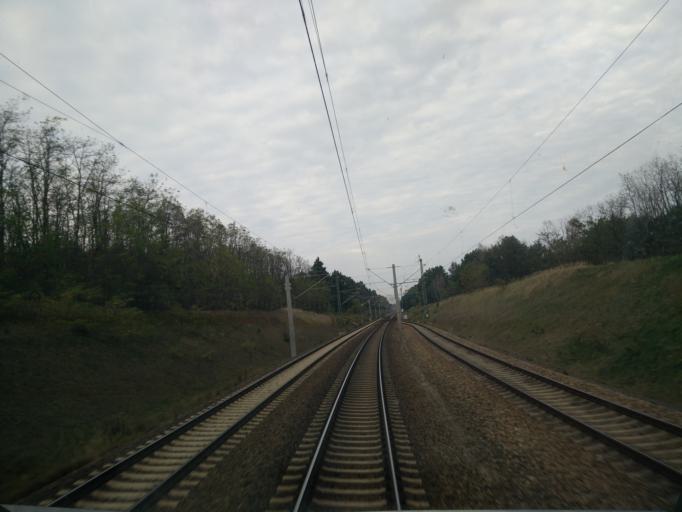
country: DE
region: Brandenburg
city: Halbe
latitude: 52.0367
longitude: 13.7186
